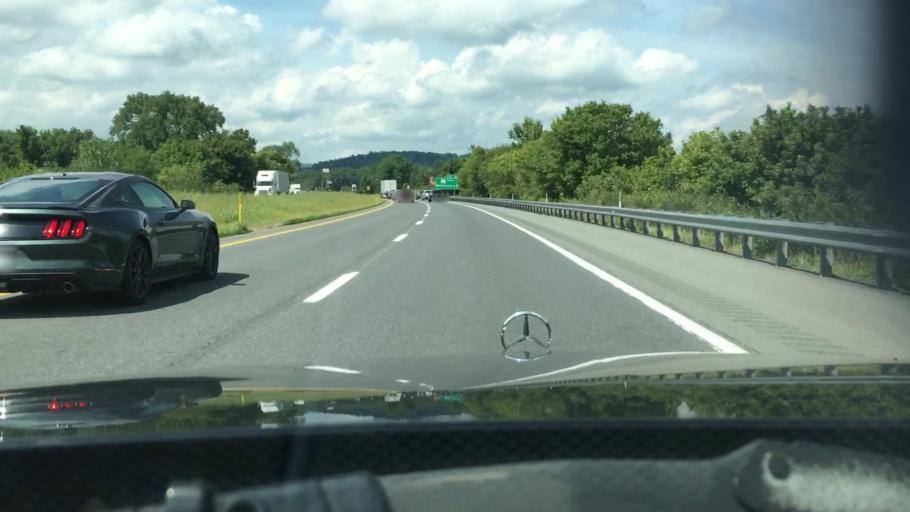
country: US
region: Maryland
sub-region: Washington County
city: Hancock
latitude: 39.7521
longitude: -78.1834
